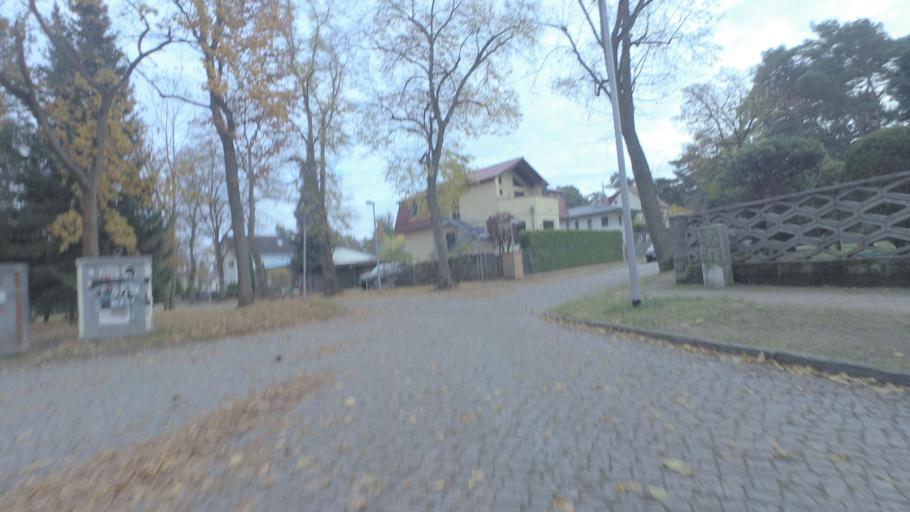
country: DE
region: Brandenburg
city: Rangsdorf
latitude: 52.2991
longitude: 13.4258
